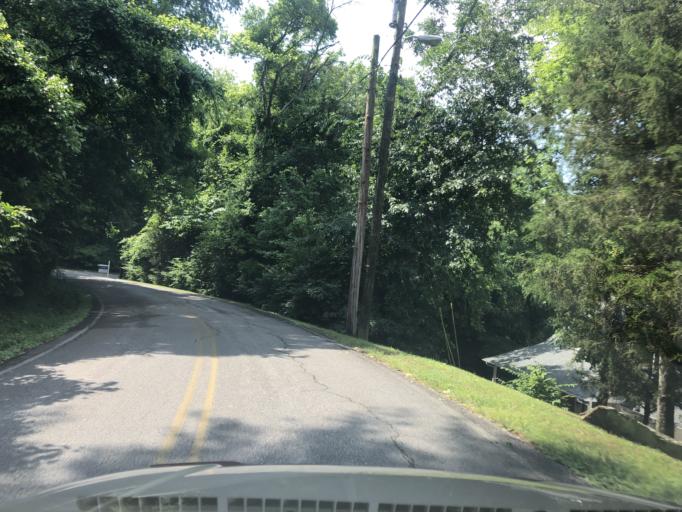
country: US
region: Tennessee
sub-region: Wilson County
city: Green Hill
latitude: 36.2408
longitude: -86.5901
